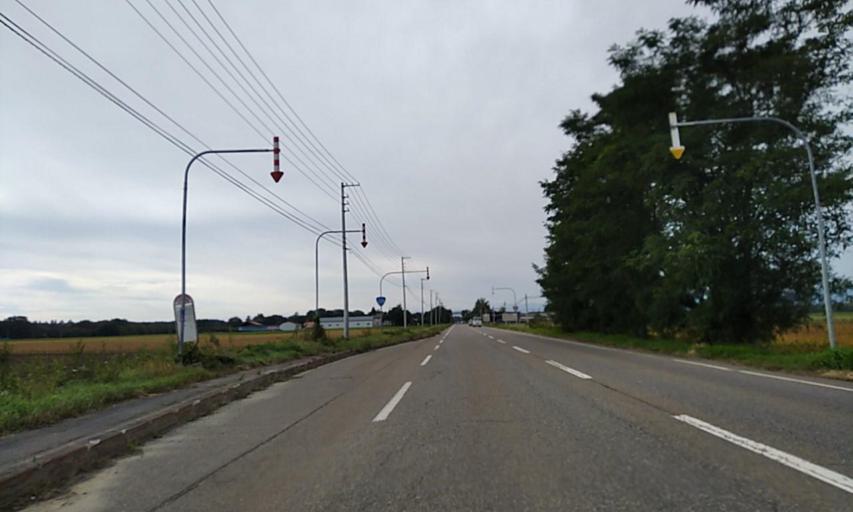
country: JP
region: Hokkaido
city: Obihiro
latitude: 42.8257
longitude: 143.1854
